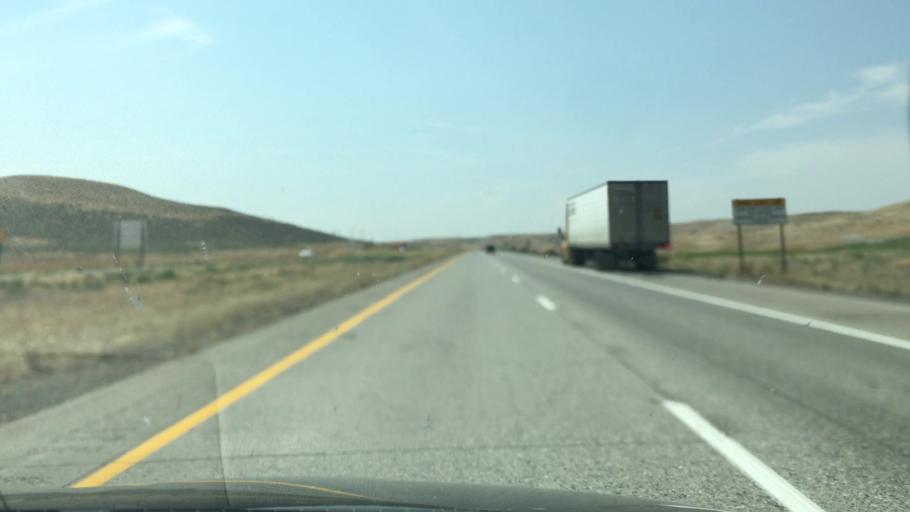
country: US
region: Idaho
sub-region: Elmore County
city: Glenns Ferry
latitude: 42.9629
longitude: -115.3174
